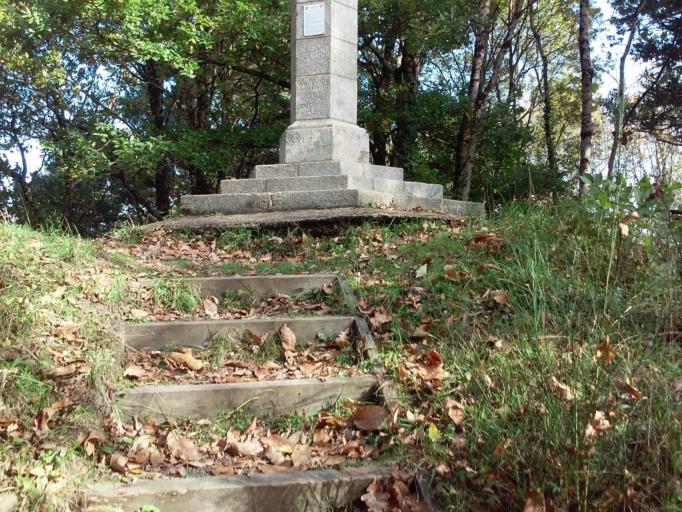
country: FR
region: Pays de la Loire
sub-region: Departement de la Vendee
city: Les Lucs-sur-Boulogne
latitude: 46.8469
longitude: -1.4866
